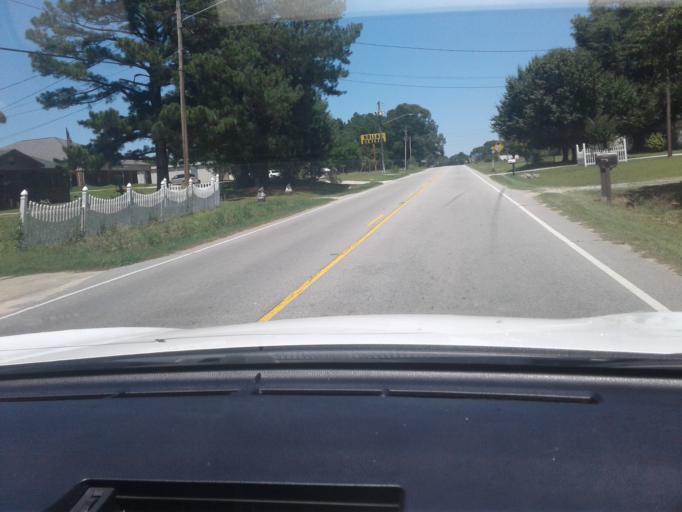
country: US
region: North Carolina
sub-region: Harnett County
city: Erwin
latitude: 35.3165
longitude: -78.6827
